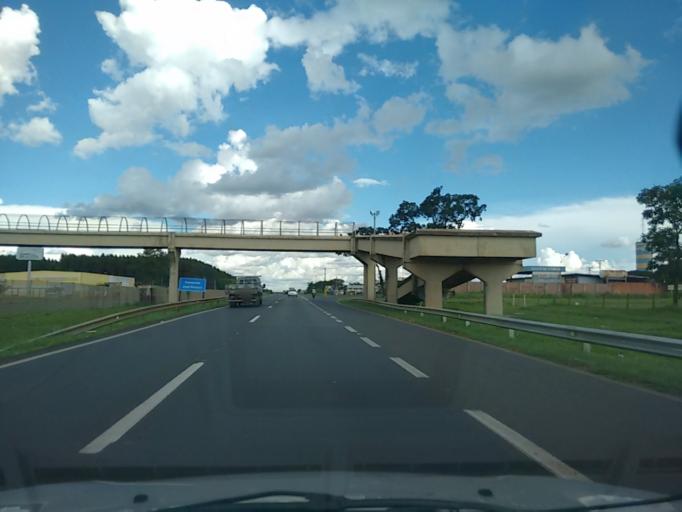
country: BR
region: Sao Paulo
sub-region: Ibate
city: Ibate
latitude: -21.9430
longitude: -48.0035
